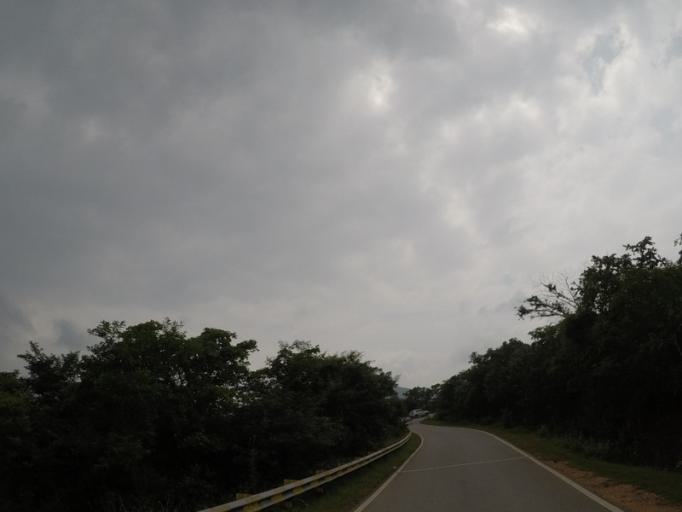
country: IN
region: Karnataka
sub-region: Chikmagalur
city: Birur
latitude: 13.5481
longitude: 75.8242
